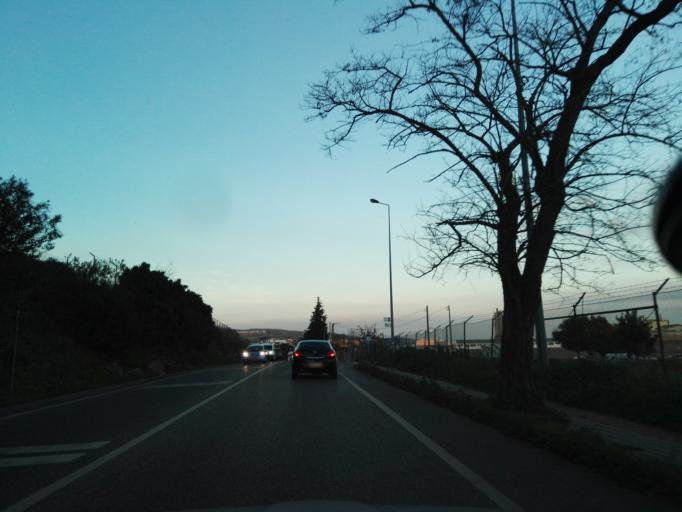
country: PT
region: Lisbon
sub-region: Vila Franca de Xira
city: Vialonga
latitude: 38.8774
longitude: -9.0521
